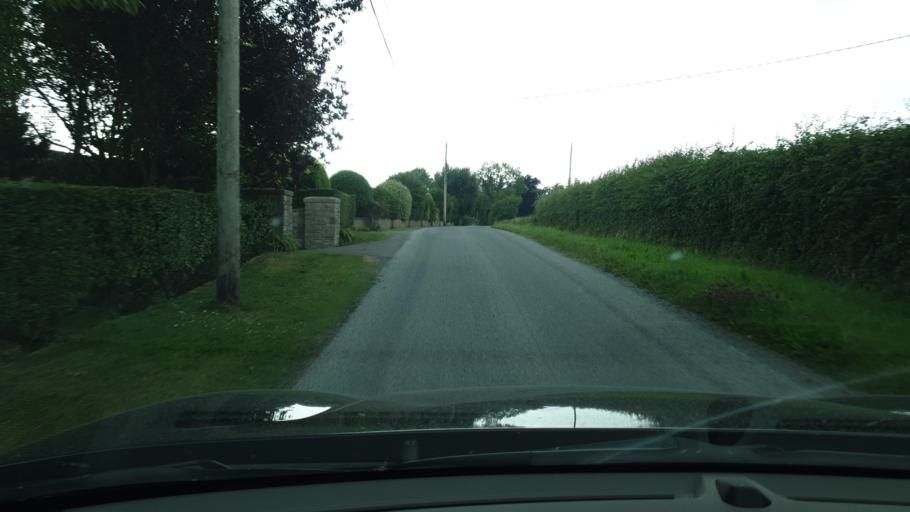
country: IE
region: Leinster
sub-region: An Mhi
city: Ratoath
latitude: 53.4930
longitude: -6.5009
